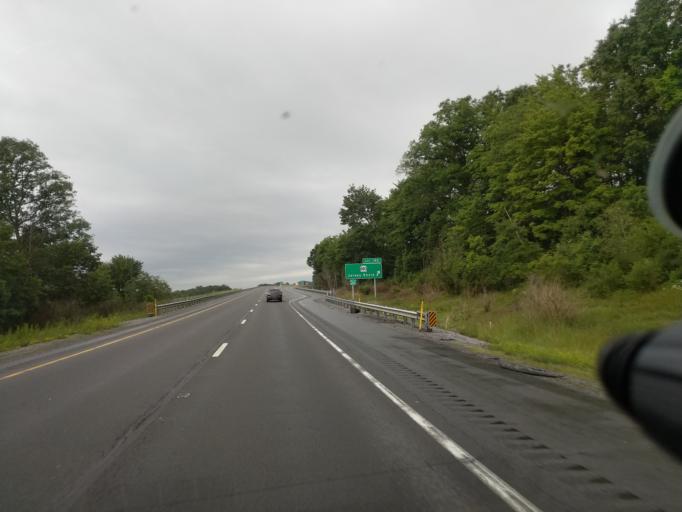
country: US
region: Pennsylvania
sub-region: Lycoming County
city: Jersey Shore
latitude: 41.0515
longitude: -77.1778
